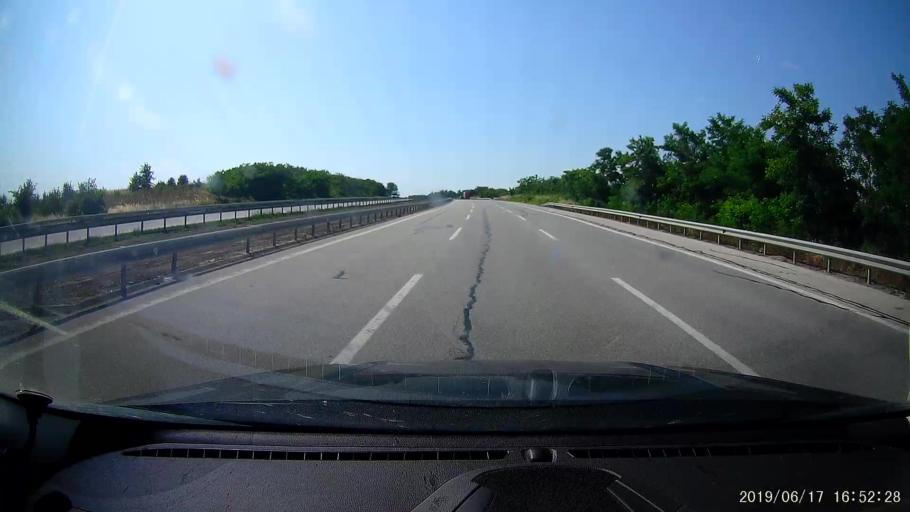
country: TR
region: Kirklareli
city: Inece
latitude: 41.5550
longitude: 27.0512
